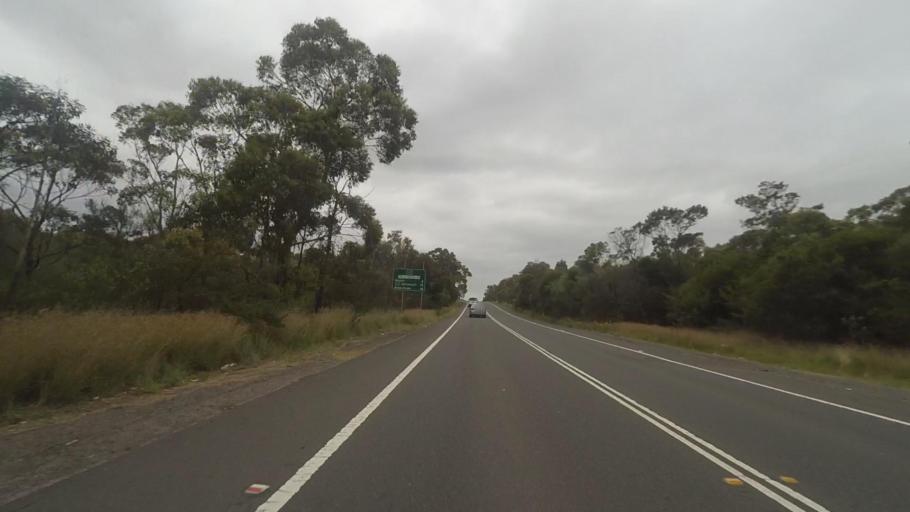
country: AU
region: New South Wales
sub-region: Sutherland Shire
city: Engadine
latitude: -34.0523
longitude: 150.9727
